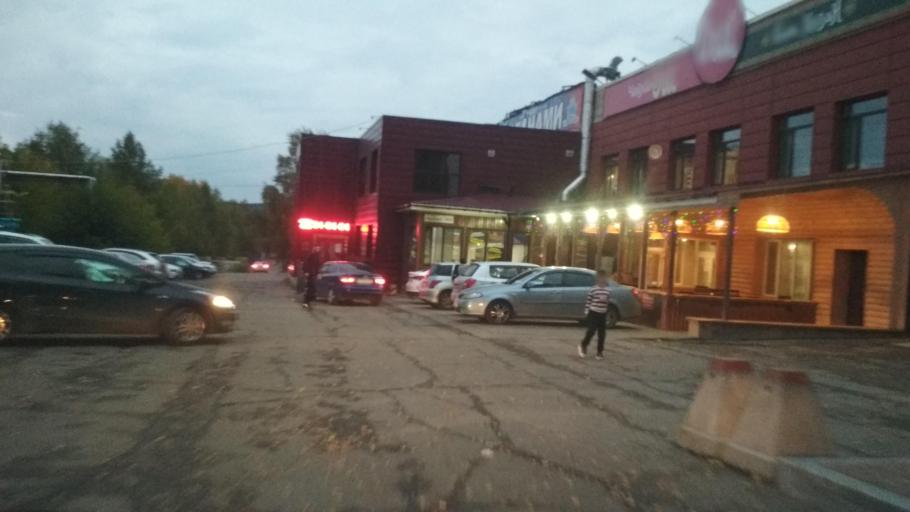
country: RU
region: Tomsk
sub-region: Tomskiy Rayon
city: Tomsk
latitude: 56.4791
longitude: 85.0199
